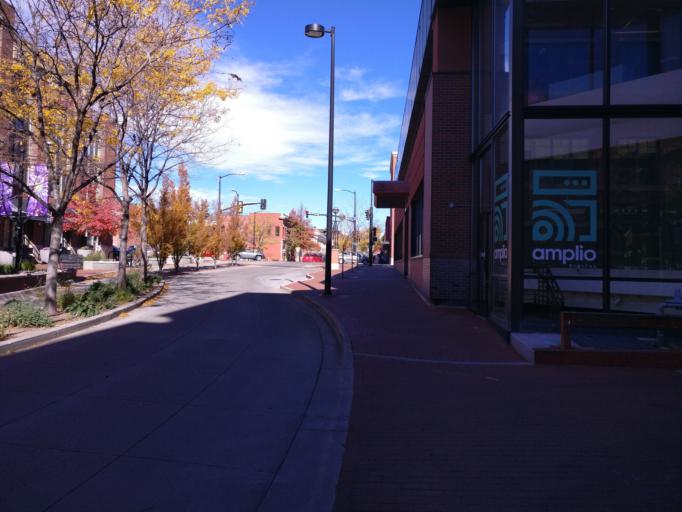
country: US
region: Colorado
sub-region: Boulder County
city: Boulder
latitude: 40.0166
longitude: -105.2781
